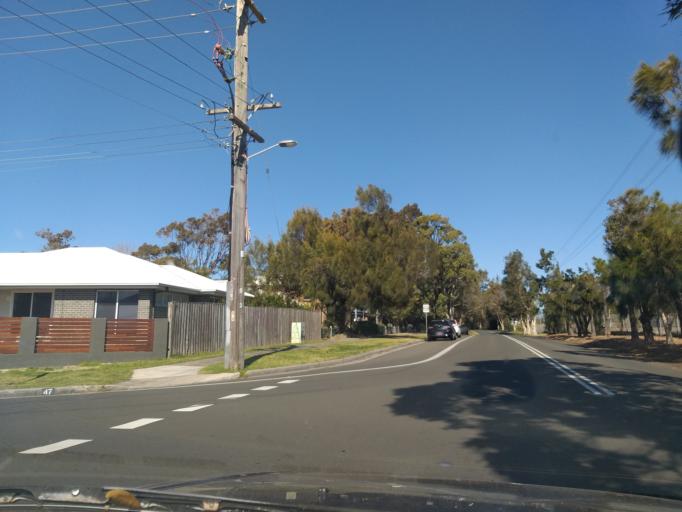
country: AU
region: New South Wales
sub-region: Wollongong
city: Bulli
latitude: -34.3543
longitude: 150.9137
